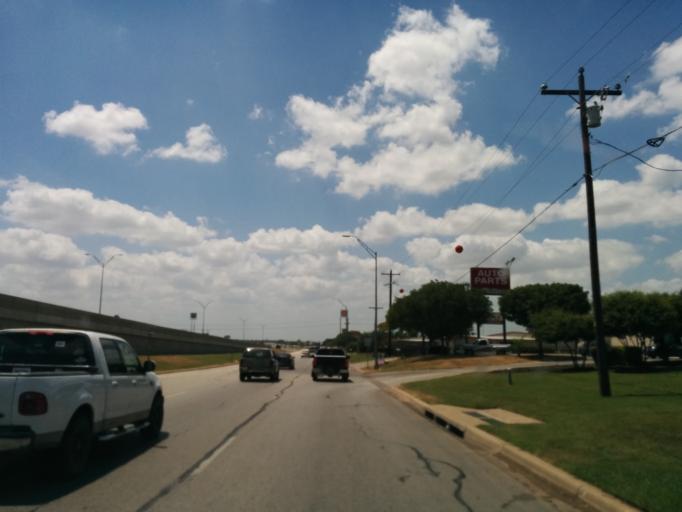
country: US
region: Texas
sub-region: Bastrop County
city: Bastrop
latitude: 30.1078
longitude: -97.3358
